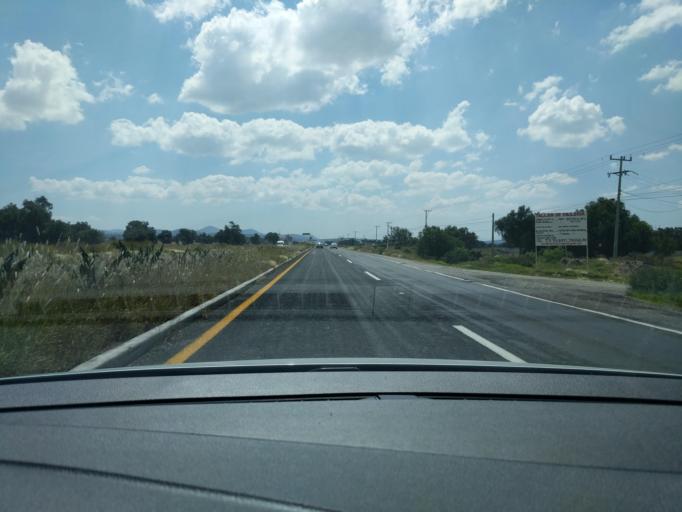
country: MX
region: Hidalgo
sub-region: Mineral de la Reforma
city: Rinconada de los Angeles
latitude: 19.9799
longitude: -98.7021
